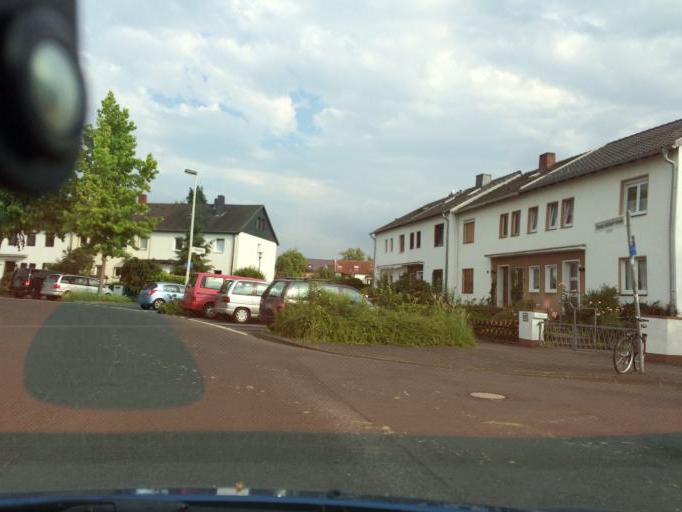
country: DE
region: North Rhine-Westphalia
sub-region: Regierungsbezirk Koln
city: Bonn
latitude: 50.7016
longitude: 7.1163
